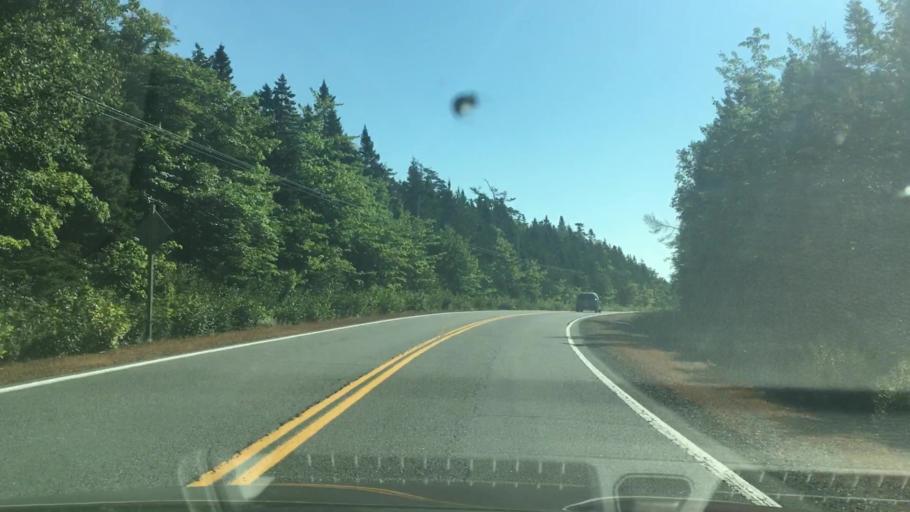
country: CA
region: Nova Scotia
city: Cole Harbour
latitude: 44.8166
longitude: -62.8814
